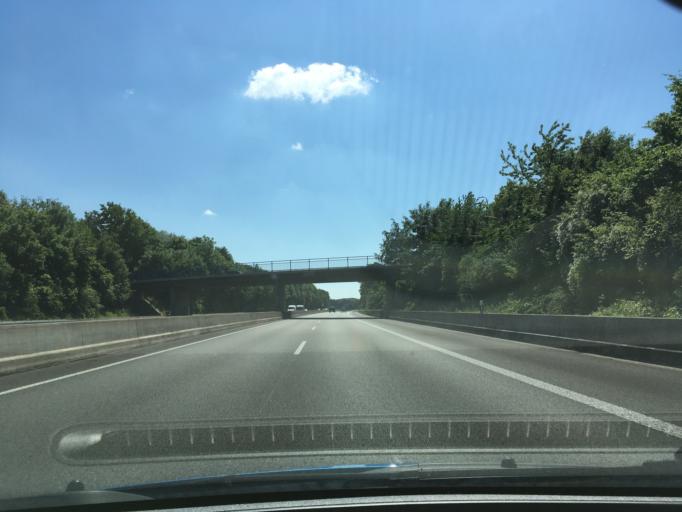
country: DE
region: North Rhine-Westphalia
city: Buende
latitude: 52.1846
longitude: 8.5869
